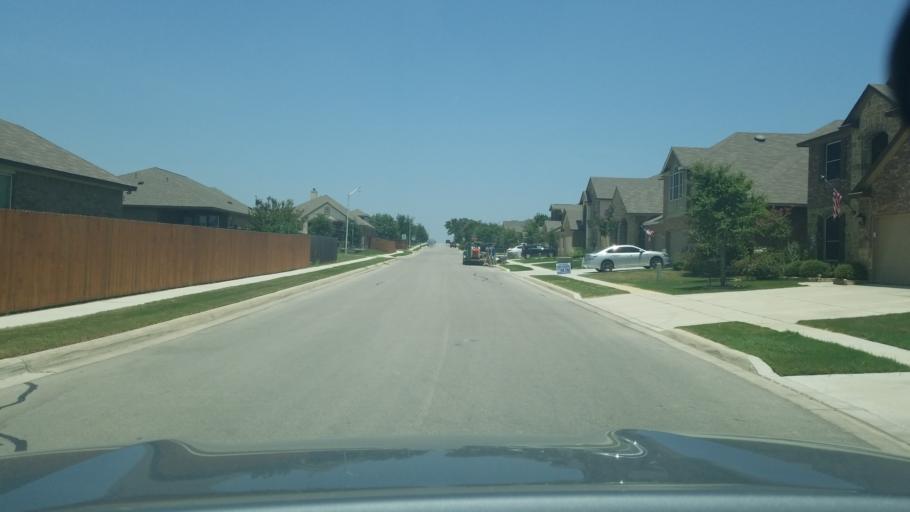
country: US
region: Texas
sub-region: Guadalupe County
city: Cibolo
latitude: 29.5785
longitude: -98.2311
